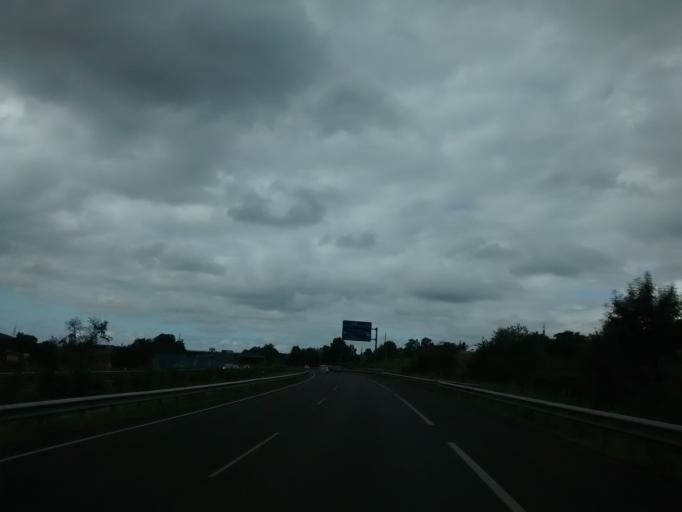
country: ES
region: Cantabria
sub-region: Provincia de Cantabria
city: Torrelavega
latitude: 43.3326
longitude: -4.0327
